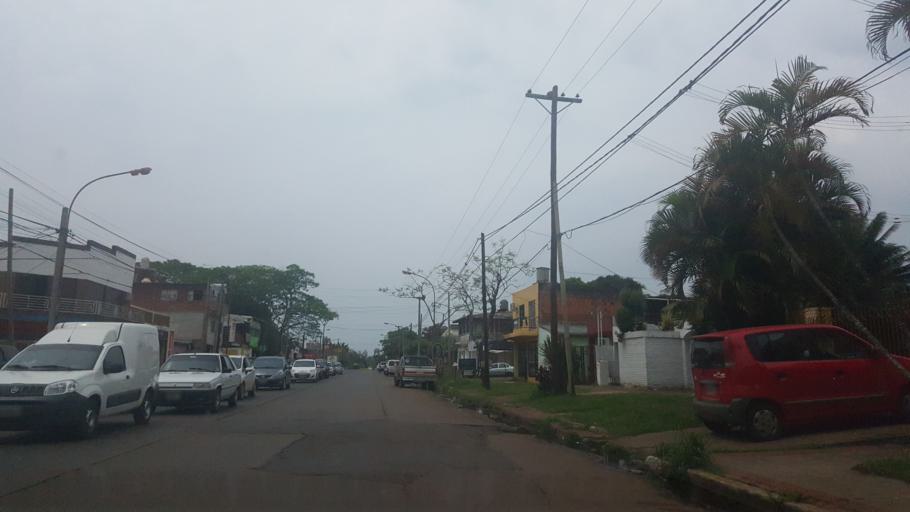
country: AR
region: Misiones
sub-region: Departamento de Capital
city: Posadas
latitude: -27.3690
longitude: -55.9162
